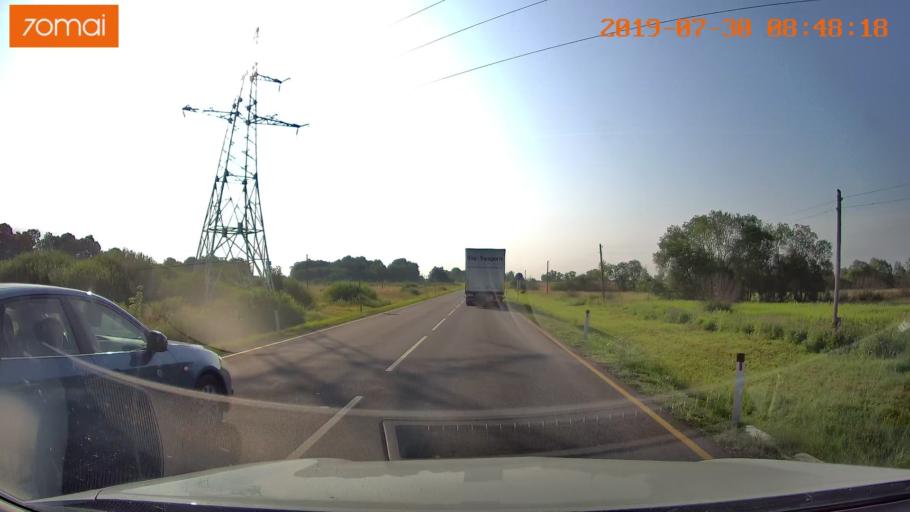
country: RU
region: Kaliningrad
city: Chernyakhovsk
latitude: 54.6185
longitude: 21.9035
